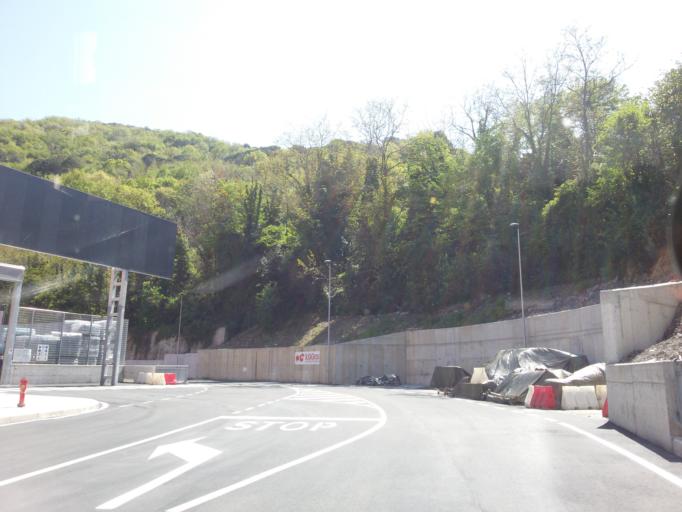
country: IT
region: Liguria
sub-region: Provincia di Genova
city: Piccarello
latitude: 44.4348
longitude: 8.9661
